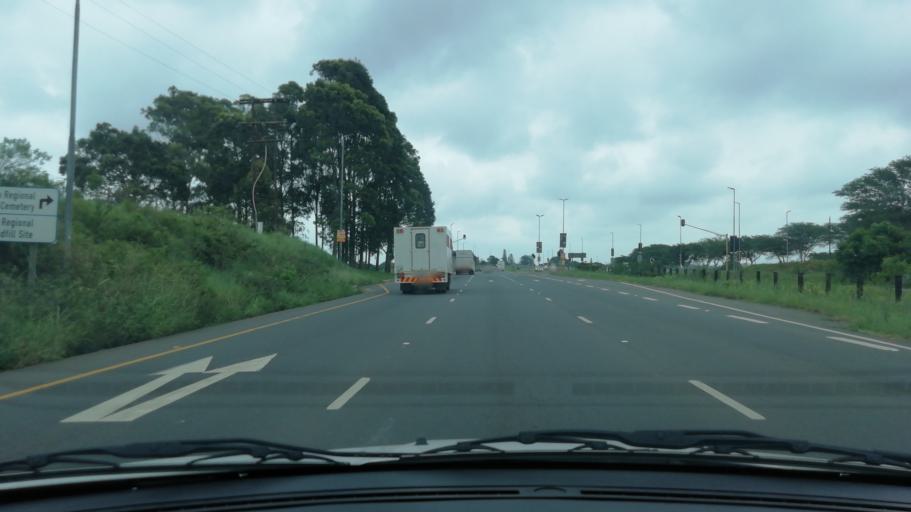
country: ZA
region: KwaZulu-Natal
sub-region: uThungulu District Municipality
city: Empangeni
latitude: -28.7670
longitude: 31.9159
